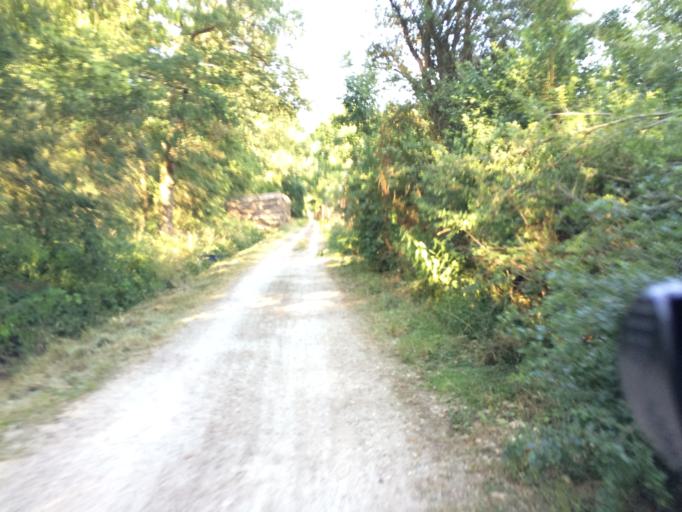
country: FR
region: Ile-de-France
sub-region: Departement de l'Essonne
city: Tigery
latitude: 48.6539
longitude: 2.5017
